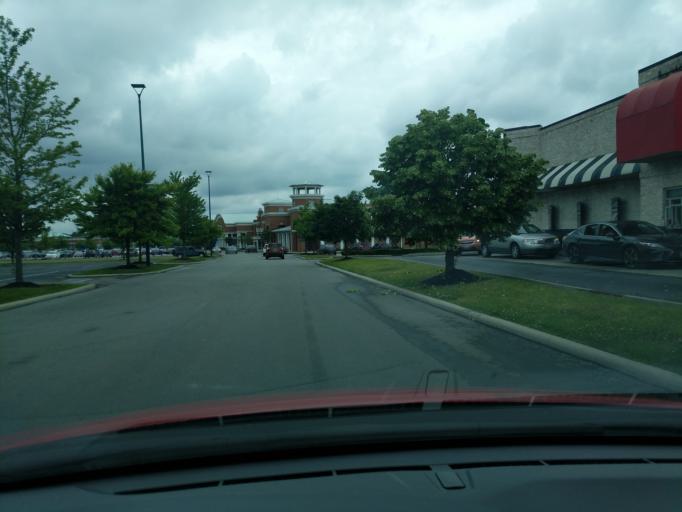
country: US
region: Ohio
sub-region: Franklin County
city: Minerva Park
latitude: 40.0526
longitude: -82.9207
